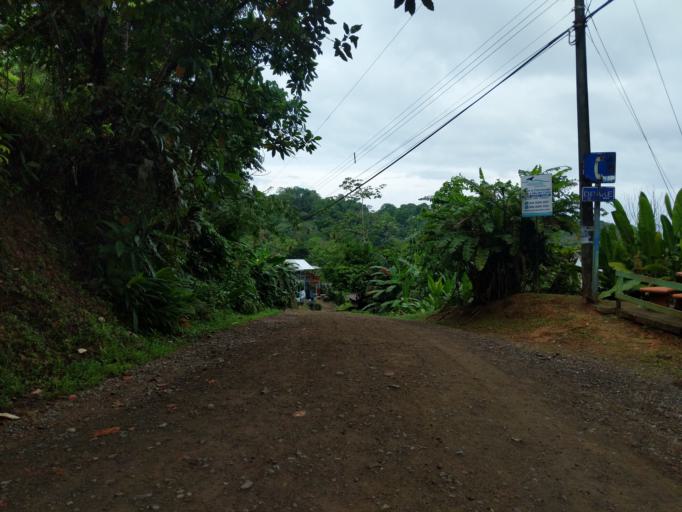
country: CR
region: Puntarenas
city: Ciudad Cortes
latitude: 8.6900
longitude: -83.6659
